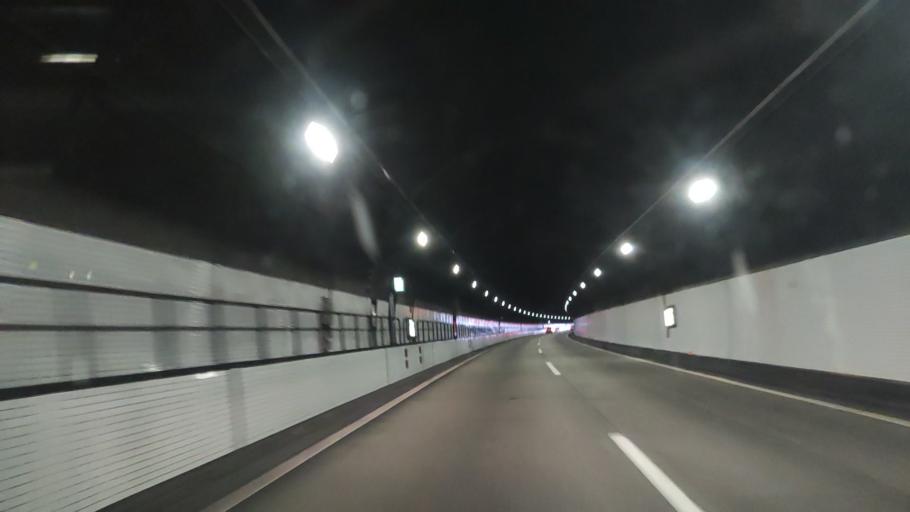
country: JP
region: Ehime
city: Niihama
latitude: 33.9163
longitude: 133.3036
